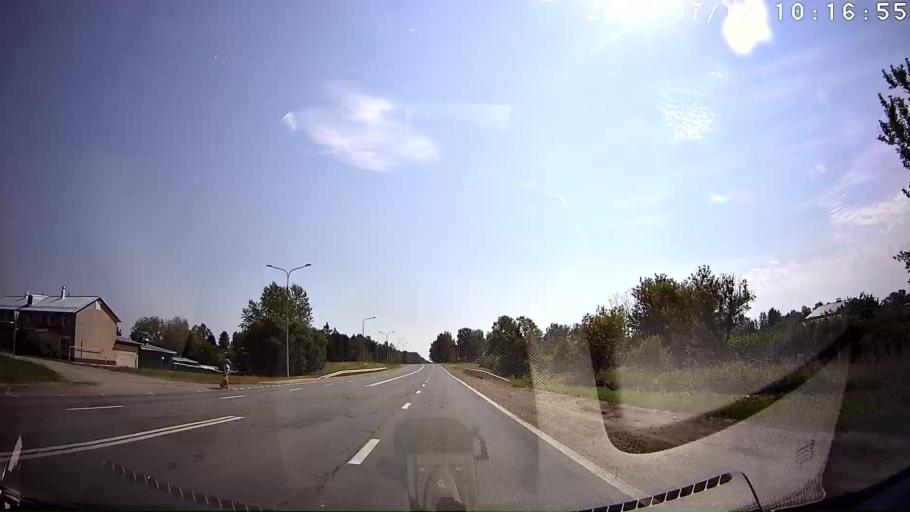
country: RU
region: Mariy-El
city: Sovetskiy
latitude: 56.7474
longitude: 48.3462
